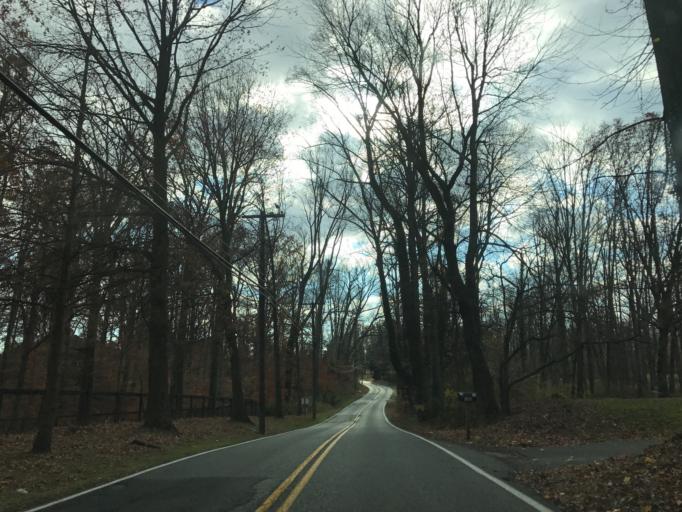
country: US
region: Maryland
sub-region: Harford County
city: Pleasant Hills
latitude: 39.5063
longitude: -76.3731
